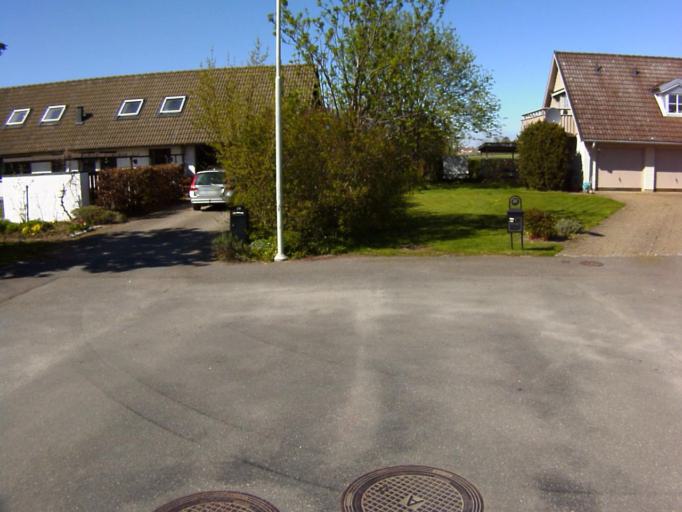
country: SE
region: Skane
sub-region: Kristianstads Kommun
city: Kristianstad
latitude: 56.0342
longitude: 14.2018
